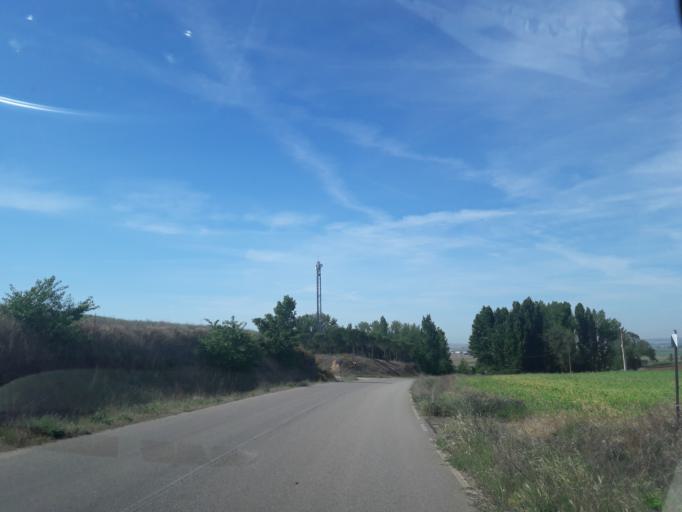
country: ES
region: Castille and Leon
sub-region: Provincia de Salamanca
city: Villoruela
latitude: 41.0149
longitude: -5.3948
